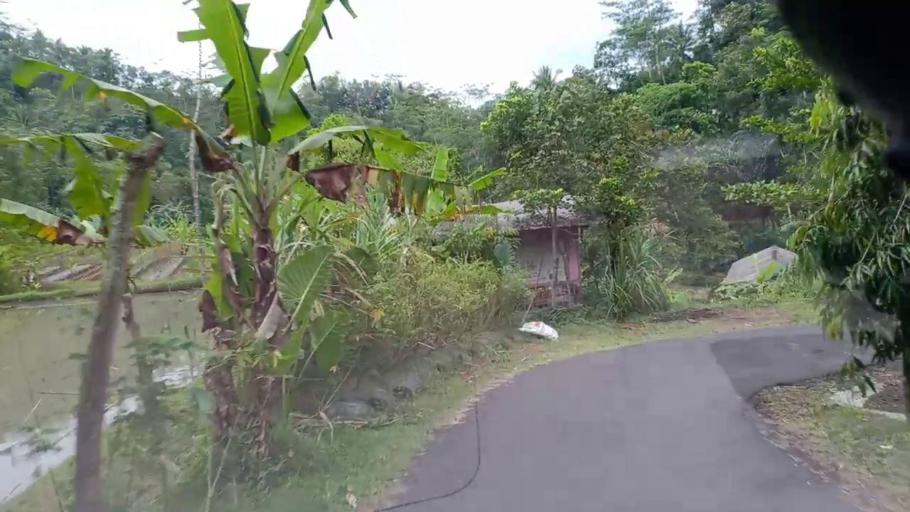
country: ID
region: West Java
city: Tangsi
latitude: -7.3402
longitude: 108.3055
